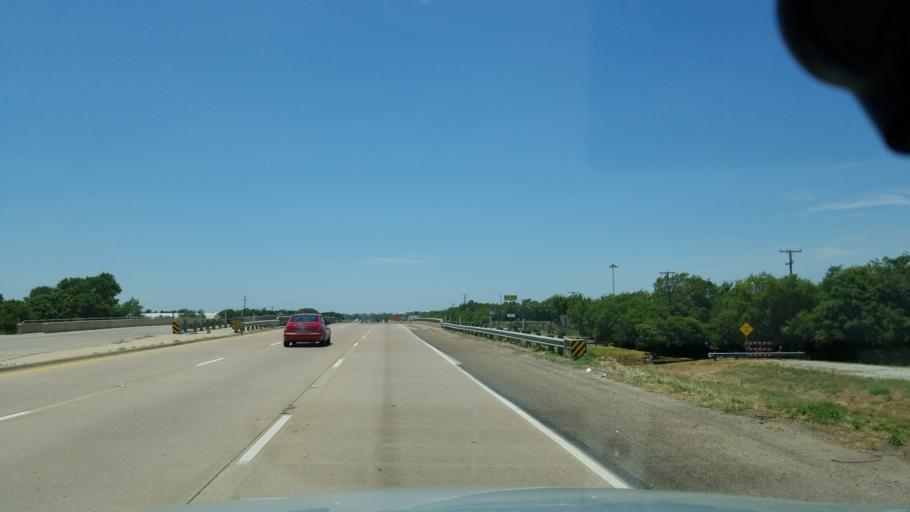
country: US
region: Texas
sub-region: Dallas County
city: Cockrell Hill
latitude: 32.7498
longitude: -96.9296
